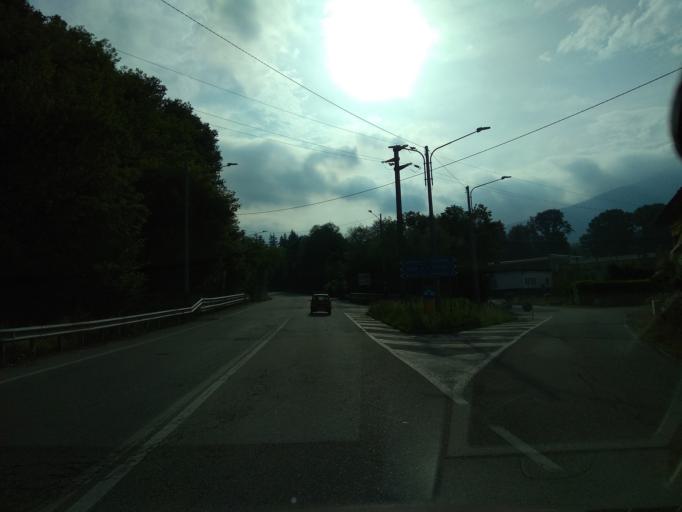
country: IT
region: Piedmont
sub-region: Provincia di Biella
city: Trivero-Prativero-Ponzone
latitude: 45.6432
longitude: 8.1644
